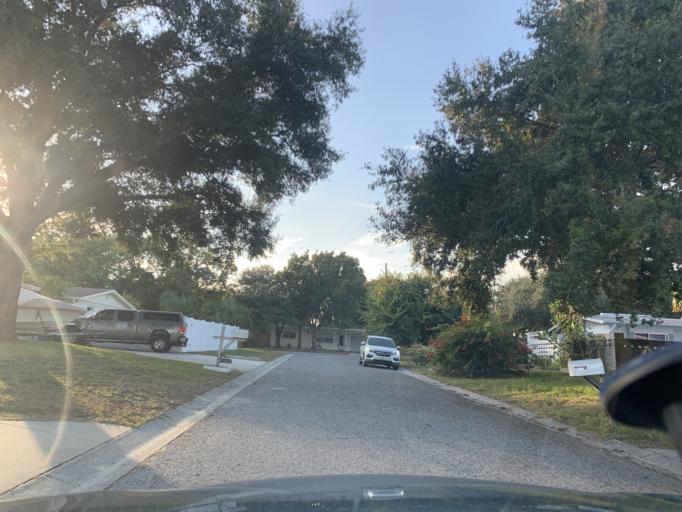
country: US
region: Florida
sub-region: Pinellas County
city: Ridgecrest
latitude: 27.8852
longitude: -82.7962
